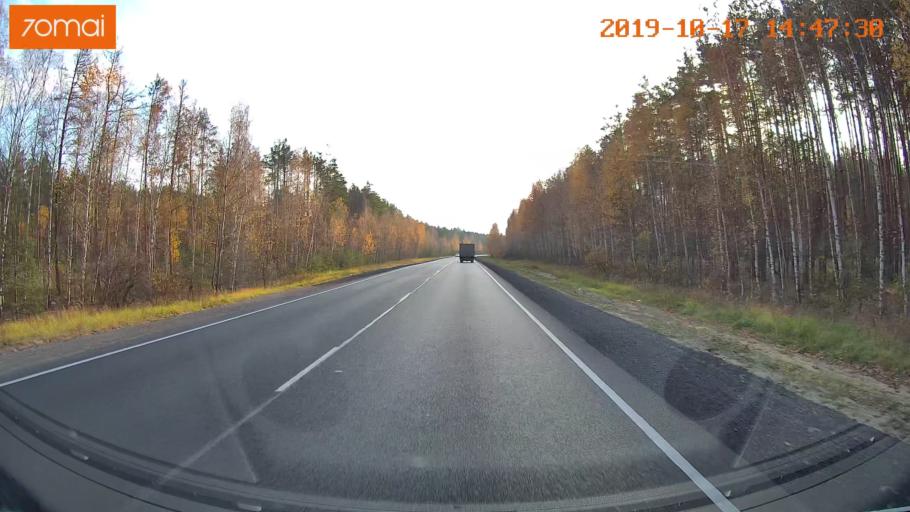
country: RU
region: Rjazan
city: Solotcha
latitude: 54.7707
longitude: 39.8596
